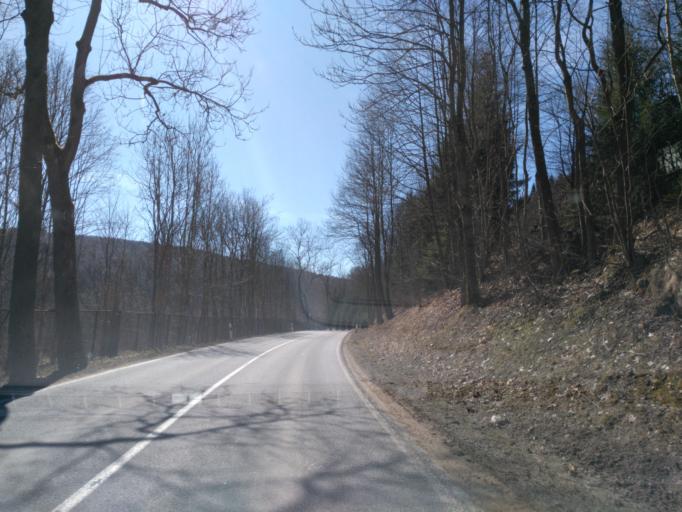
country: CZ
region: Ustecky
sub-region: Okres Chomutov
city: Vejprty
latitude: 50.4568
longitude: 13.0211
